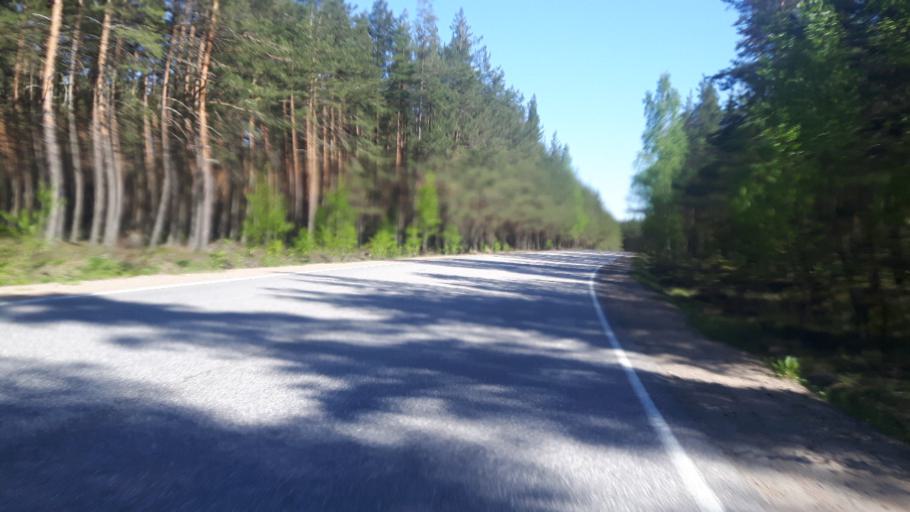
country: RU
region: Leningrad
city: Glebychevo
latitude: 60.2790
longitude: 28.8951
